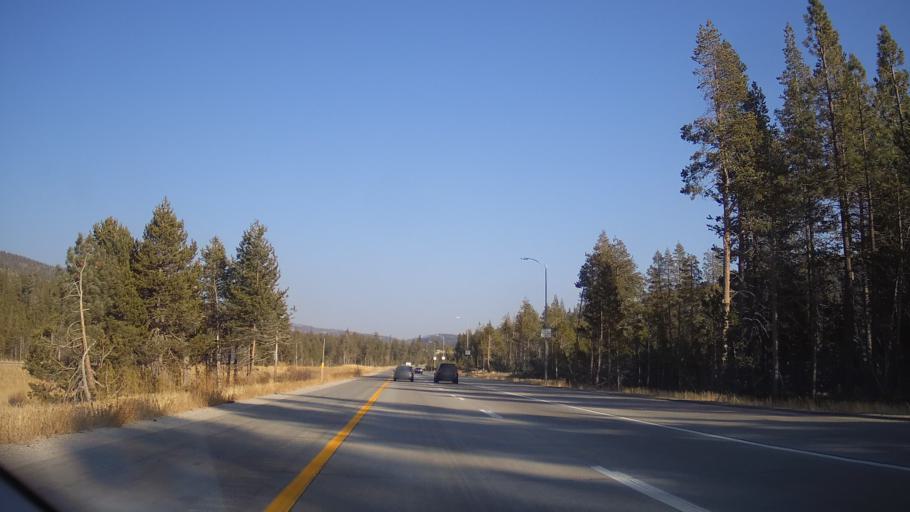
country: US
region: California
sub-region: Nevada County
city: Truckee
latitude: 39.3127
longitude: -120.4829
